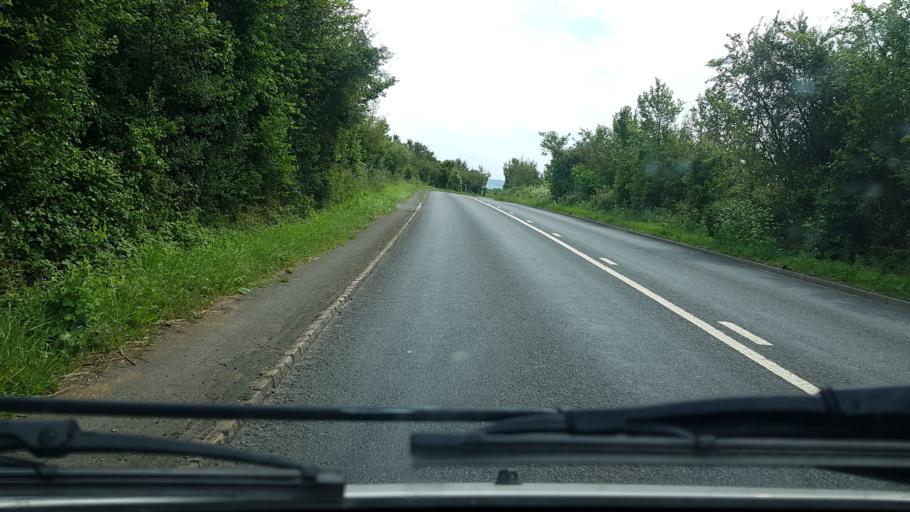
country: GB
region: England
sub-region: Worcestershire
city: Badsey
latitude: 52.0573
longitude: -1.8872
